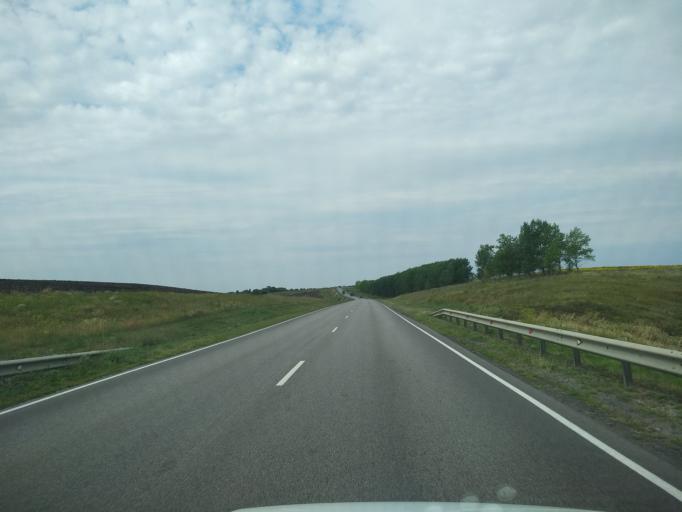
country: RU
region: Voronezj
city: Pereleshinskiy
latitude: 51.8572
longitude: 40.3427
